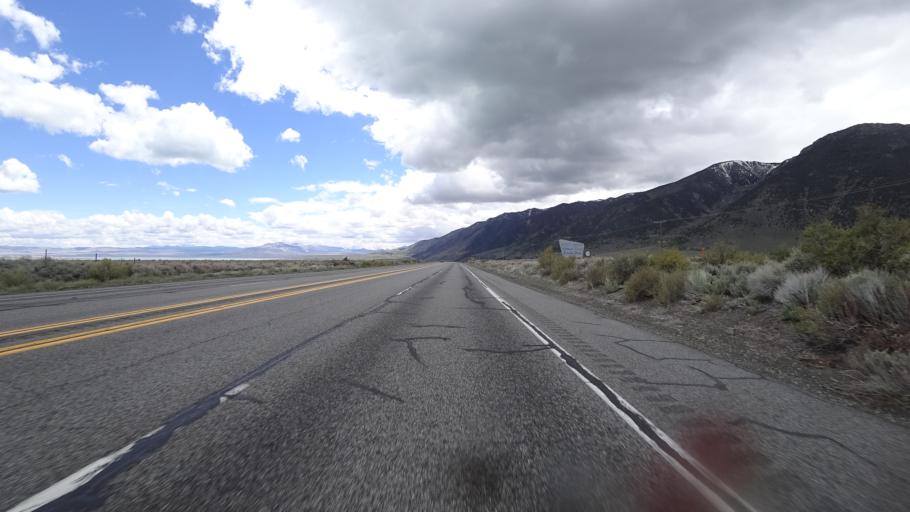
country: US
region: California
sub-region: Mono County
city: Bridgeport
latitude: 38.0303
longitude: -119.1564
